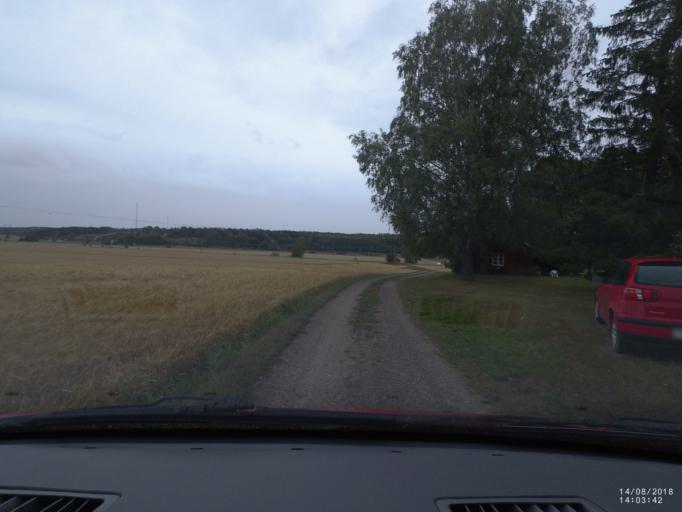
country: SE
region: Soedermanland
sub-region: Nykopings Kommun
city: Nykoping
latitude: 58.7535
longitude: 16.9612
